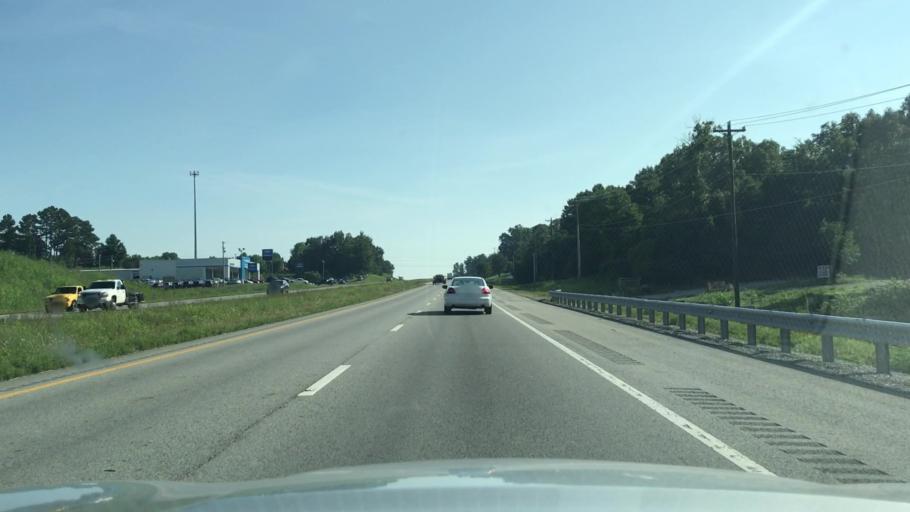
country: US
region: Tennessee
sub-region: Overton County
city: Livingston
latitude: 36.3342
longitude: -85.3531
